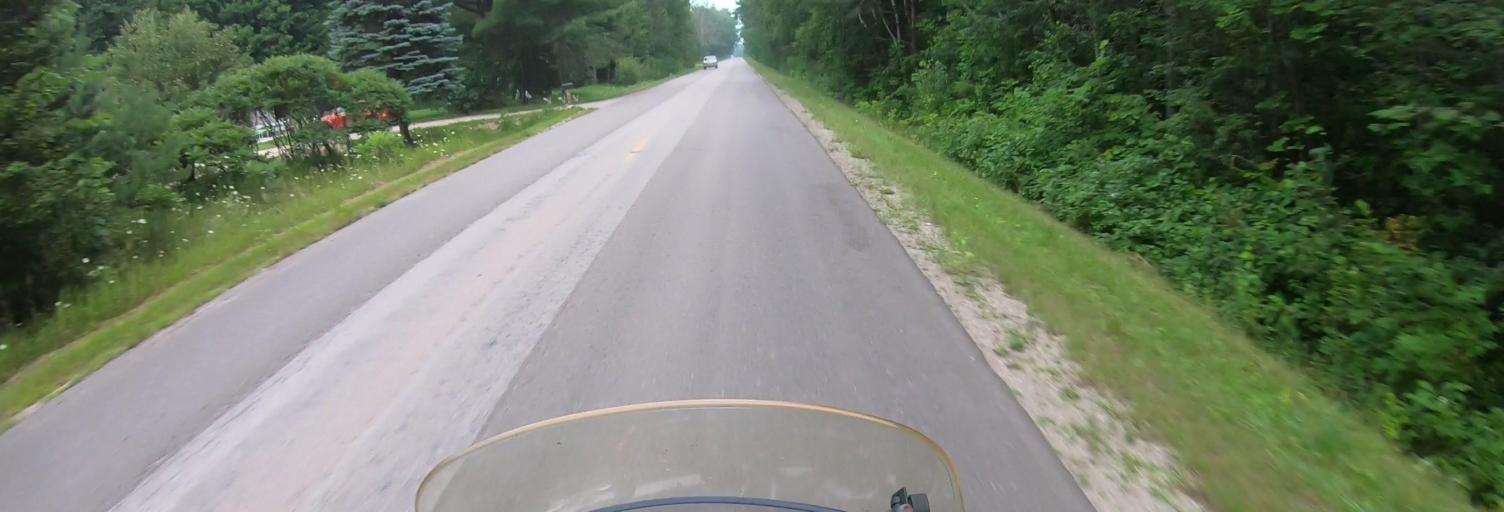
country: US
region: Michigan
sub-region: Mackinac County
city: Saint Ignace
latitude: 45.6945
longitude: -84.8207
